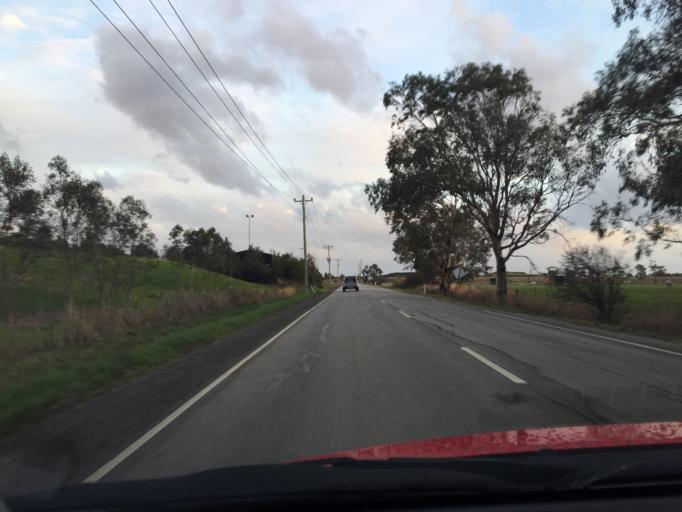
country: AU
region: Victoria
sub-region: Frankston
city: Sandhurst
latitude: -38.0378
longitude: 145.1874
